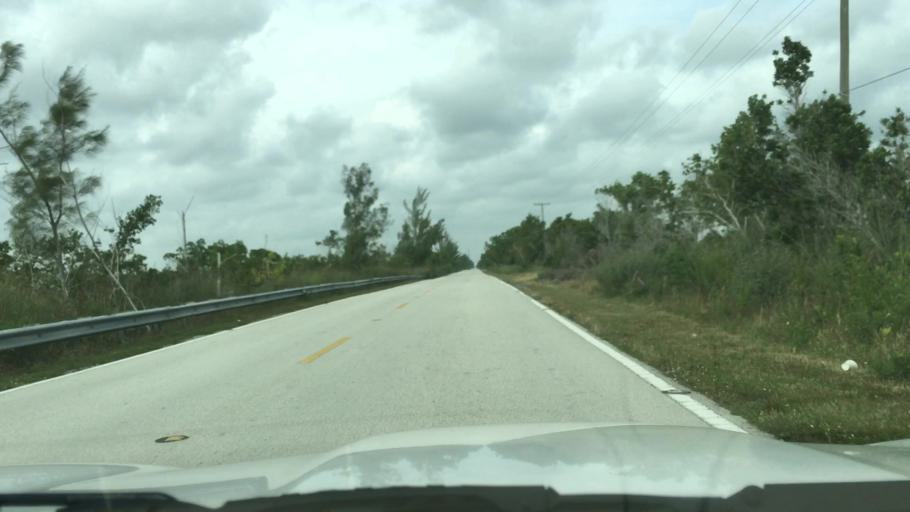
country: US
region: Florida
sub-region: Miami-Dade County
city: Florida City
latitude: 25.3504
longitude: -80.4190
